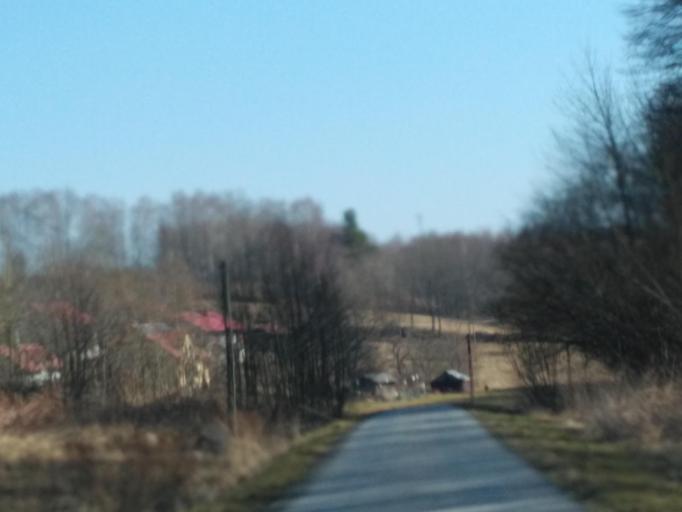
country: PL
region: Subcarpathian Voivodeship
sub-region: Powiat ropczycko-sedziszowski
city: Iwierzyce
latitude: 49.9565
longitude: 21.7331
